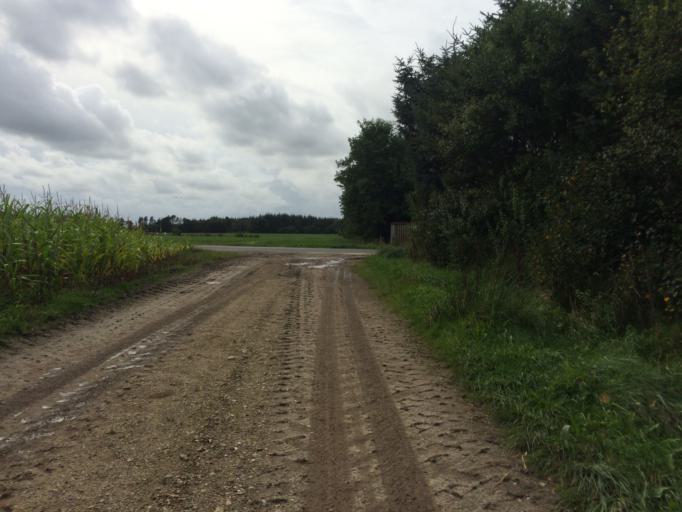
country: DK
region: Central Jutland
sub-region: Holstebro Kommune
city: Ulfborg
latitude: 56.2271
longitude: 8.3845
